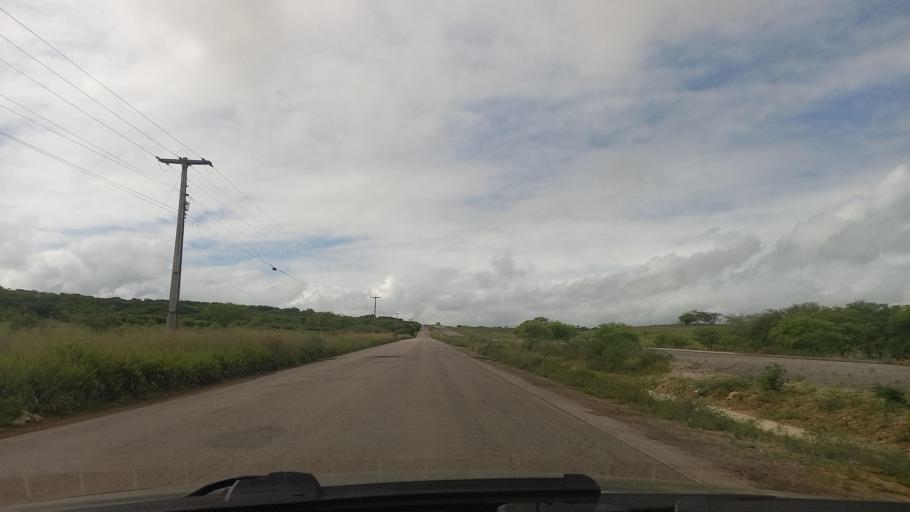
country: BR
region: Alagoas
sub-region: Batalha
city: Batalha
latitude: -9.6582
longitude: -37.1746
